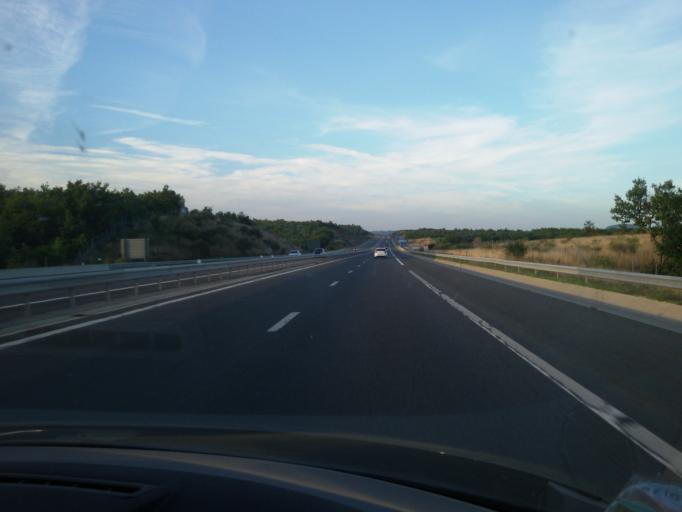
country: FR
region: Midi-Pyrenees
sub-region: Departement de l'Aveyron
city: Creissels
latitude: 44.1545
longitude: 3.0200
